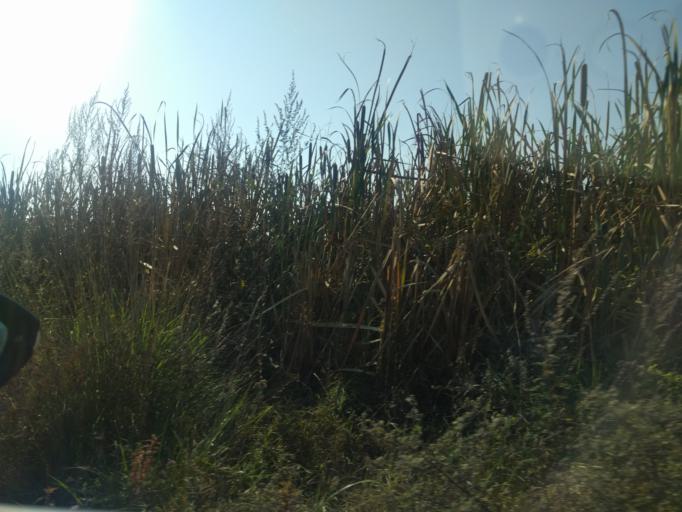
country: XK
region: Pristina
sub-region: Komuna e Gracanices
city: Glanica
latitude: 42.5850
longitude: 21.0227
